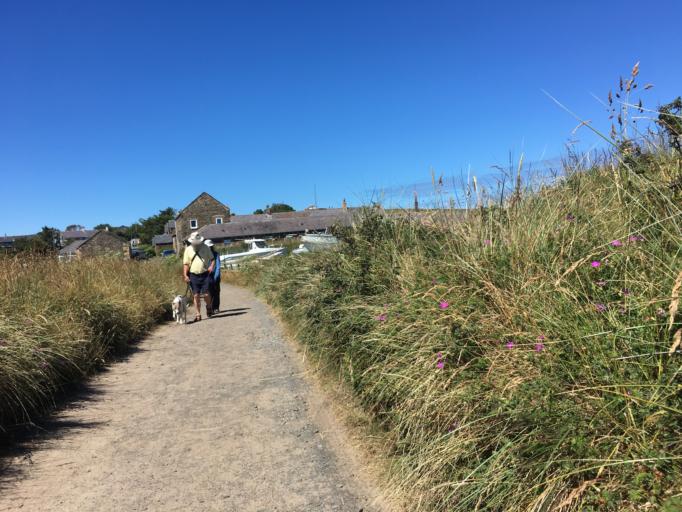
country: GB
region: England
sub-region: Northumberland
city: Embleton
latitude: 55.5128
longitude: -1.6191
